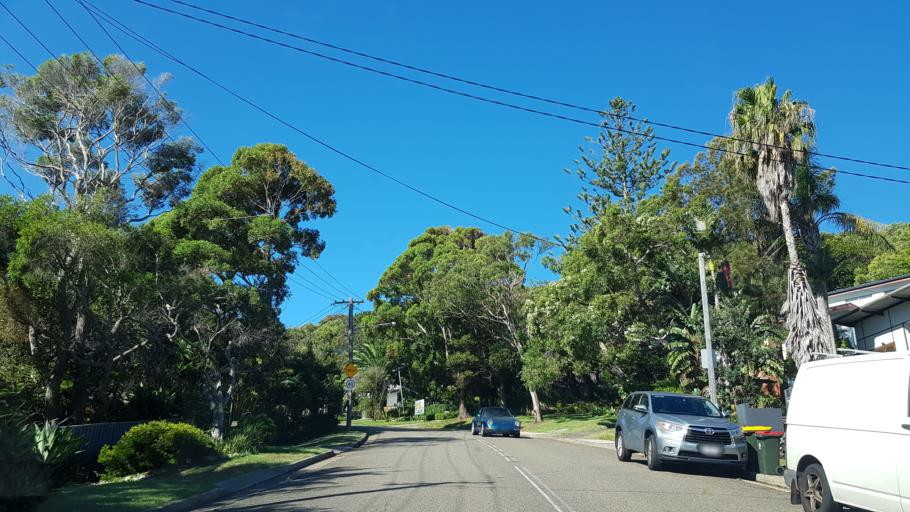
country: AU
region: New South Wales
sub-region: Pittwater
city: Bilgola Beach
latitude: -33.6227
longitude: 151.3373
